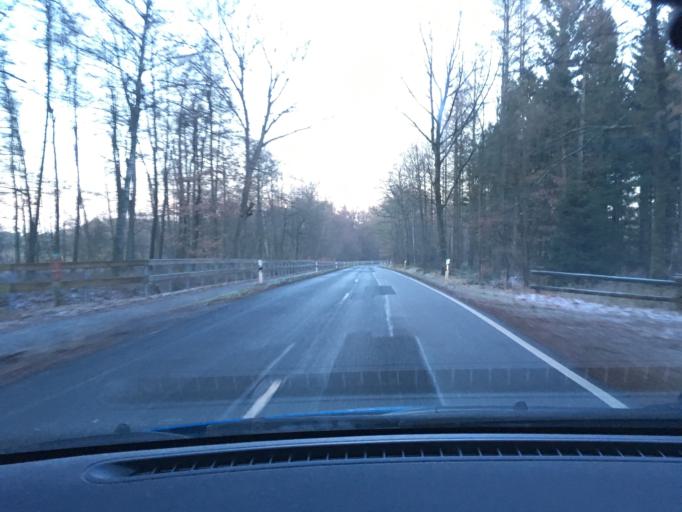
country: DE
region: Lower Saxony
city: Handeloh
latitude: 53.2514
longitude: 9.8775
